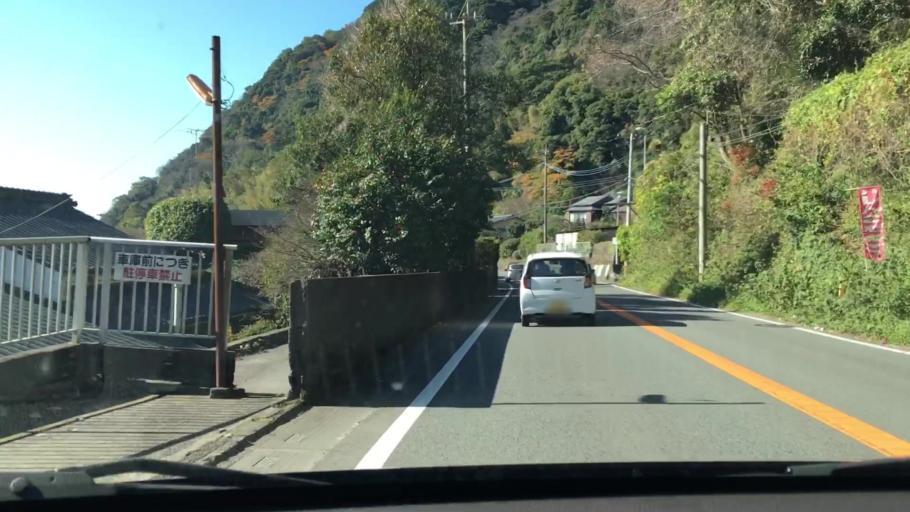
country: JP
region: Kagoshima
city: Kagoshima-shi
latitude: 31.6233
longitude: 130.5872
